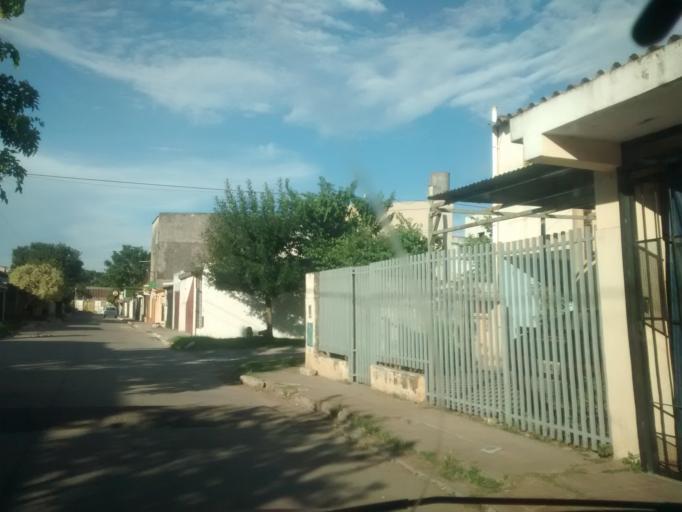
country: AR
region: Chaco
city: Fontana
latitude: -27.4495
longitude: -59.0157
